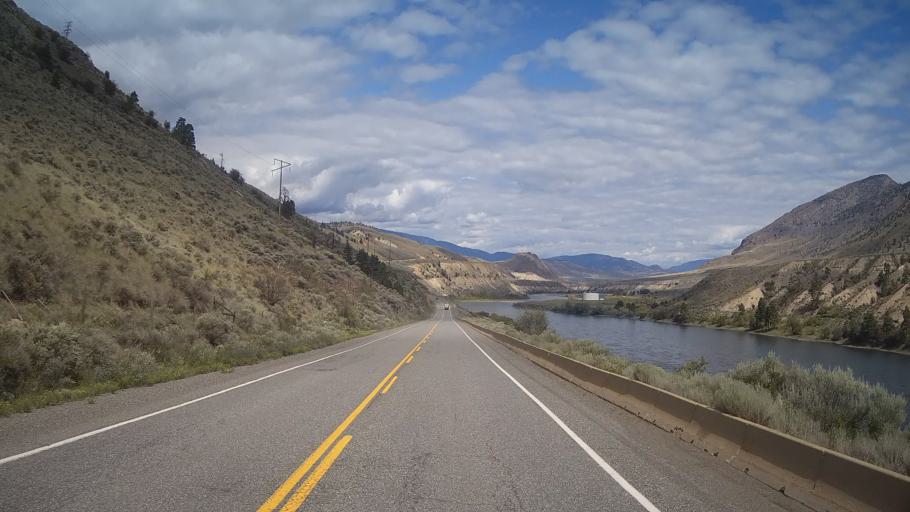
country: CA
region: British Columbia
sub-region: Thompson-Nicola Regional District
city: Ashcroft
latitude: 50.5448
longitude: -121.2913
